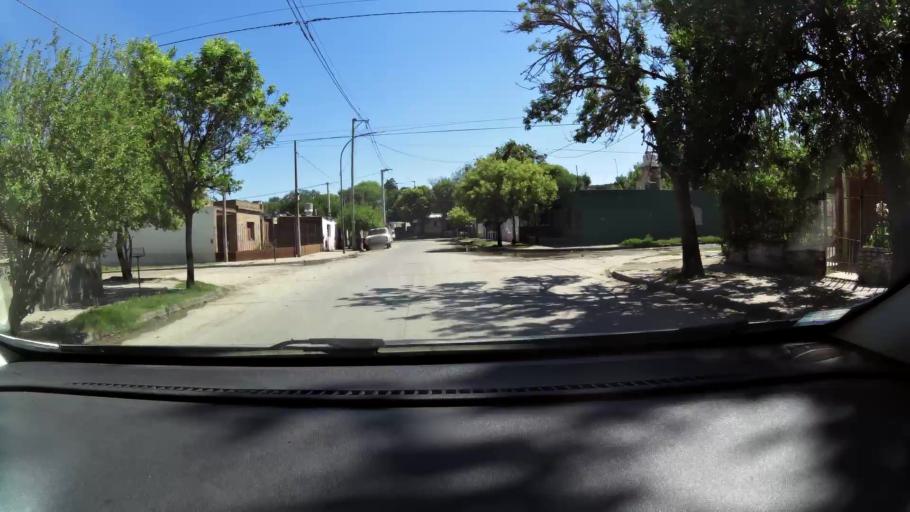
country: AR
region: Cordoba
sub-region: Departamento de Capital
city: Cordoba
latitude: -31.4121
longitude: -64.1362
